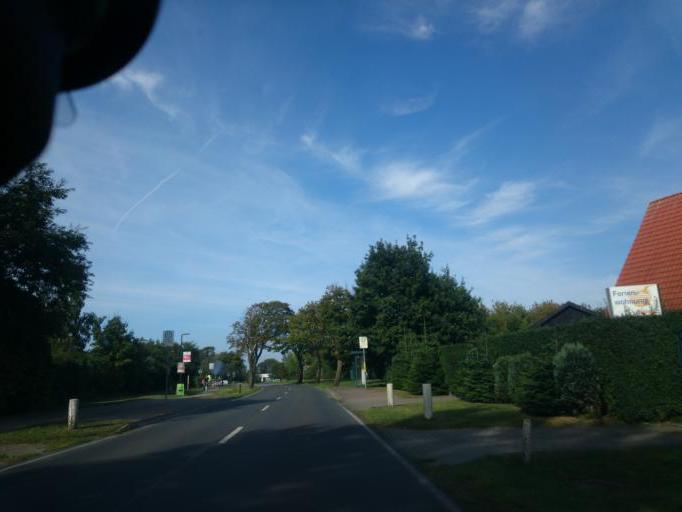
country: DE
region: Mecklenburg-Vorpommern
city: Elmenhorst
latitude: 54.1436
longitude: 12.0272
